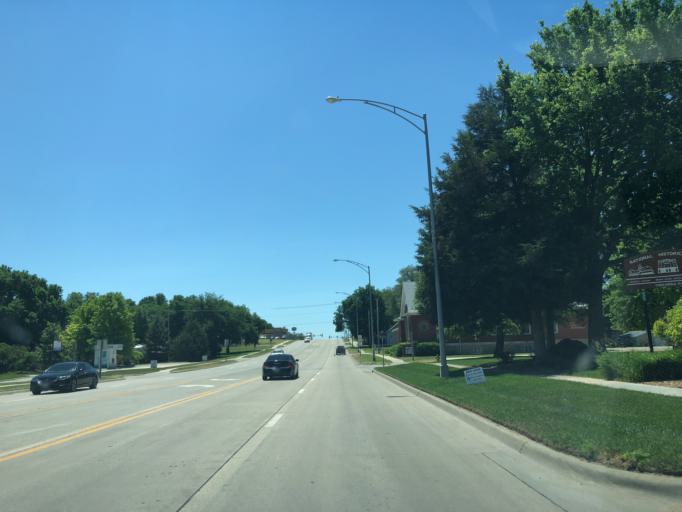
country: US
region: Kansas
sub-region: Cloud County
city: Concordia
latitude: 39.5702
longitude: -97.6575
